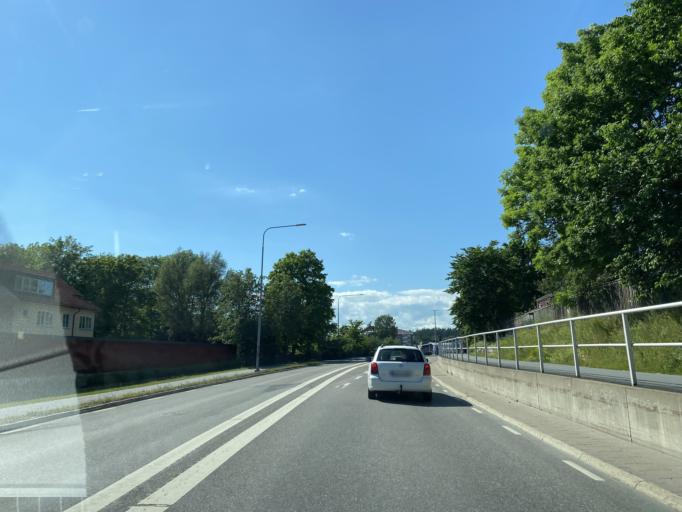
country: SE
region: Stockholm
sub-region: Norrtalje Kommun
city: Norrtalje
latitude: 59.7591
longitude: 18.6942
